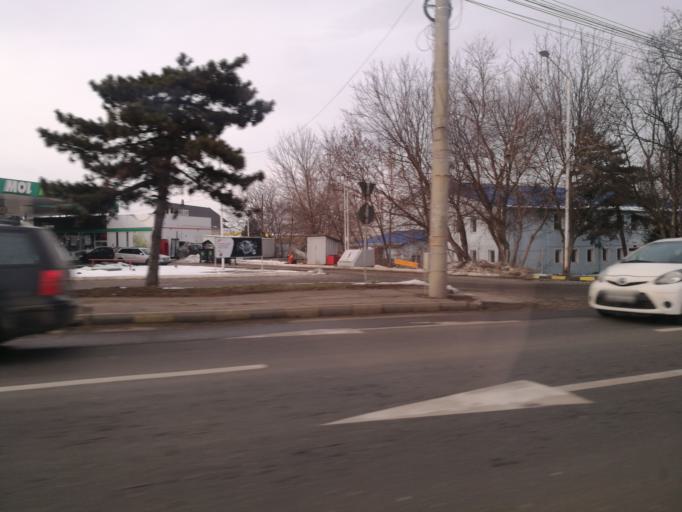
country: RO
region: Suceava
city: Suceava
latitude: 47.6557
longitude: 26.2615
